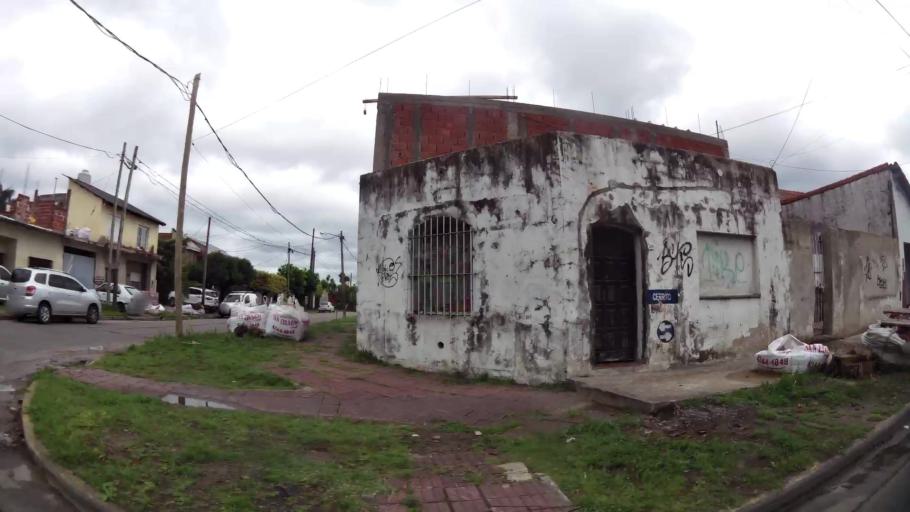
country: AR
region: Buenos Aires
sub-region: Partido de Lomas de Zamora
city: Lomas de Zamora
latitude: -34.7548
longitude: -58.3740
